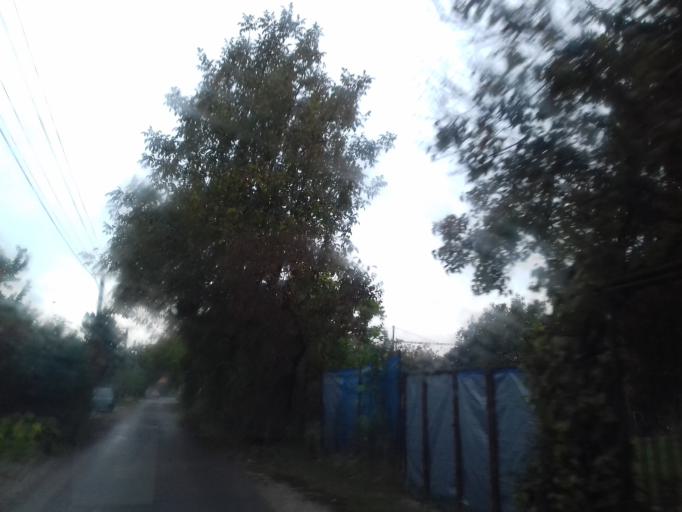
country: SK
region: Bratislavsky
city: Bratislava
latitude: 48.1419
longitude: 17.1830
